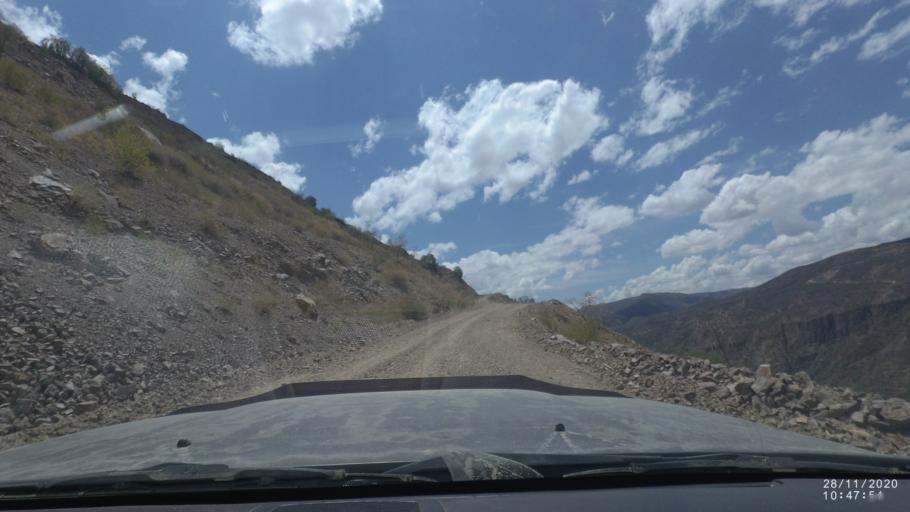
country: BO
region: Cochabamba
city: Capinota
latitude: -17.7860
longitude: -66.1242
